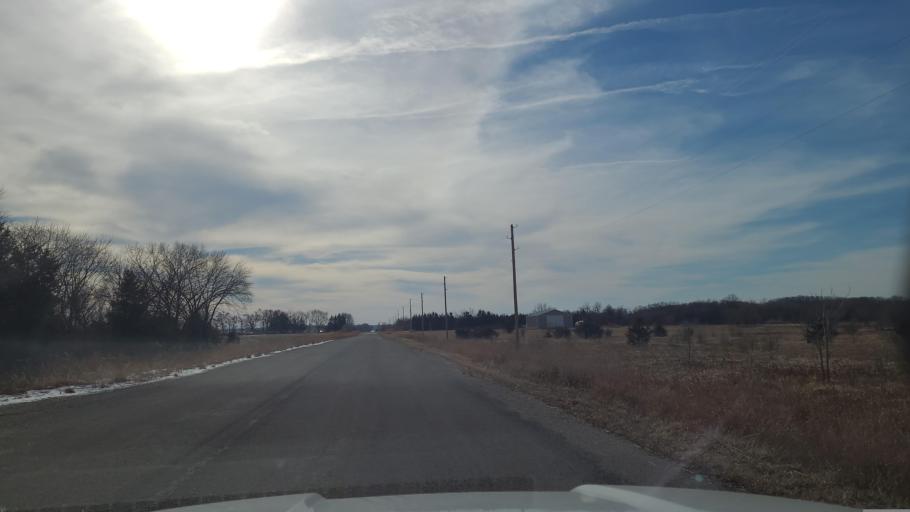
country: US
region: Kansas
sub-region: Douglas County
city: Lawrence
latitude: 38.9057
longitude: -95.2052
